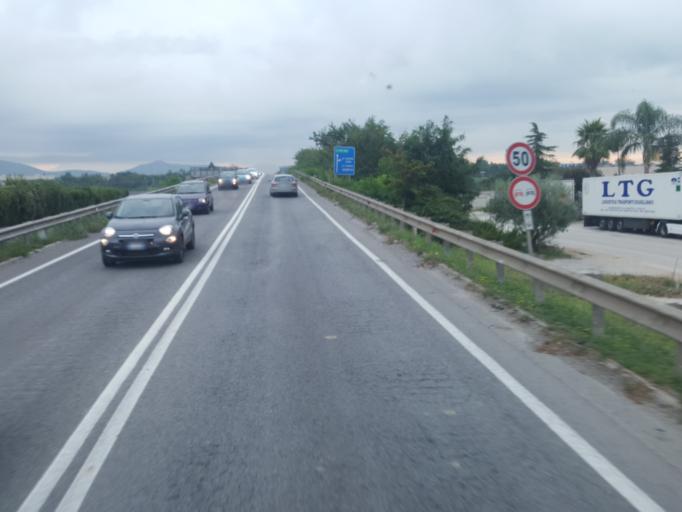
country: IT
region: Campania
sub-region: Provincia di Caserta
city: Pignataro Maggiore
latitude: 41.1639
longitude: 14.1662
